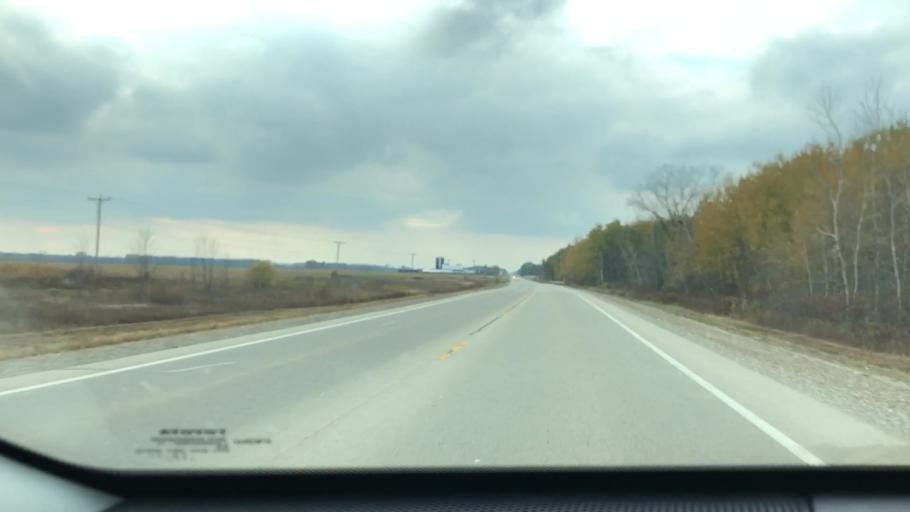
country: US
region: Wisconsin
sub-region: Brown County
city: Oneida
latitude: 44.5024
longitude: -88.2407
